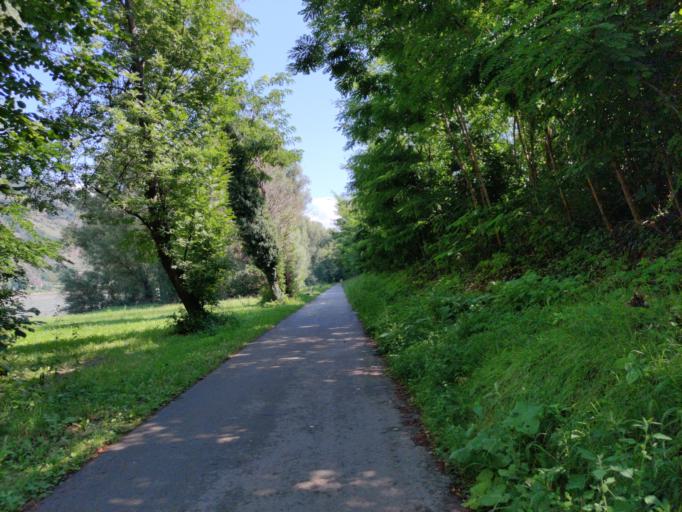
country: AT
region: Lower Austria
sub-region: Politischer Bezirk Krems
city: Spitz
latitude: 48.3624
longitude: 15.4237
